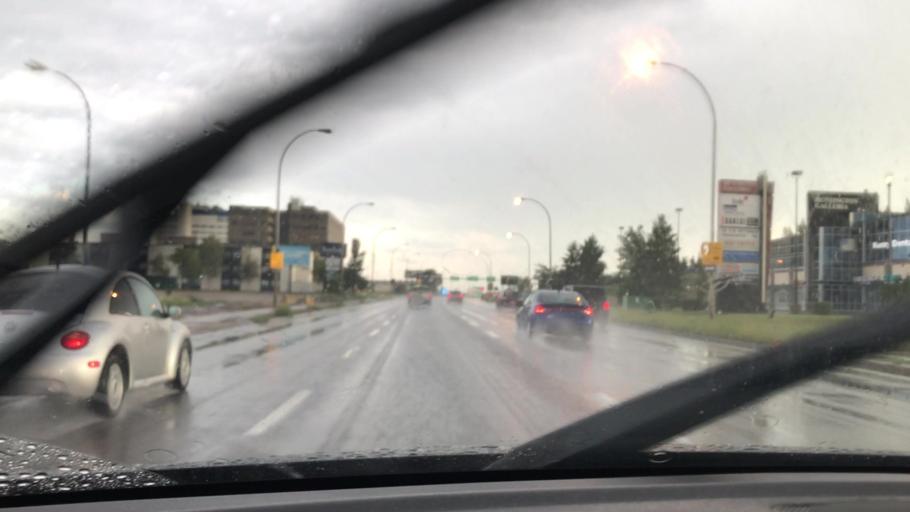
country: CA
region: Alberta
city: Edmonton
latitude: 53.4854
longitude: -113.4949
